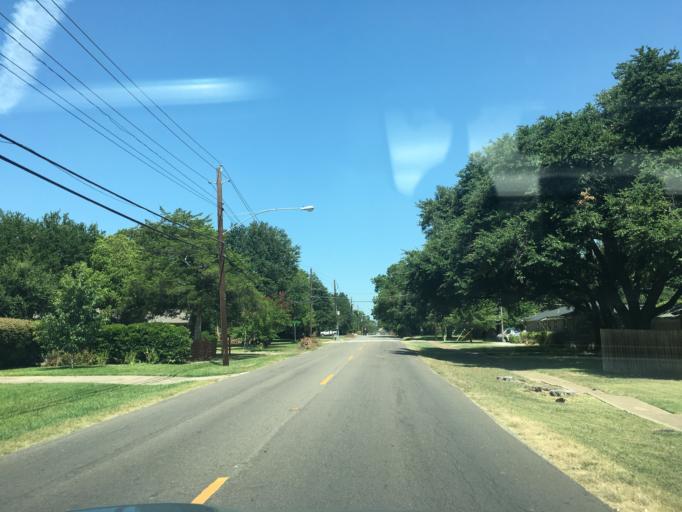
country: US
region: Texas
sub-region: Dallas County
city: Highland Park
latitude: 32.8497
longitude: -96.7453
